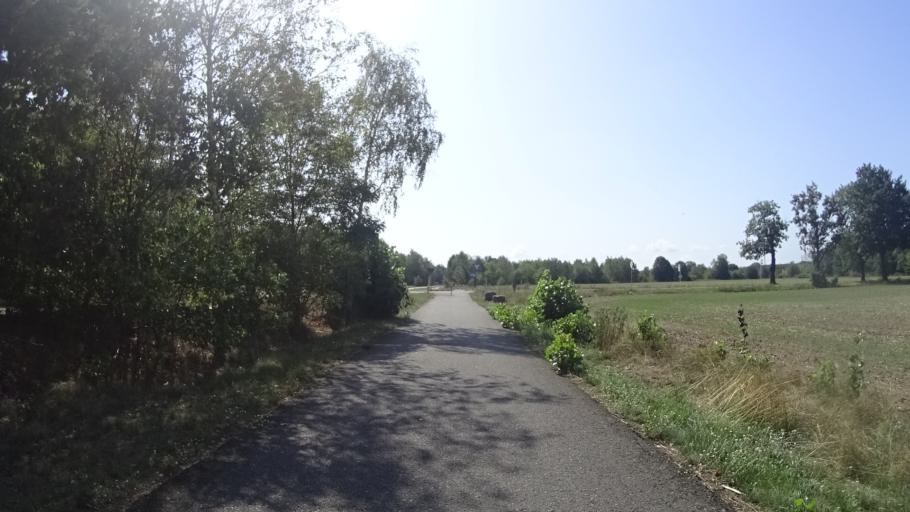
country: DE
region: Brandenburg
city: Cottbus
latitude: 51.7830
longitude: 14.3067
